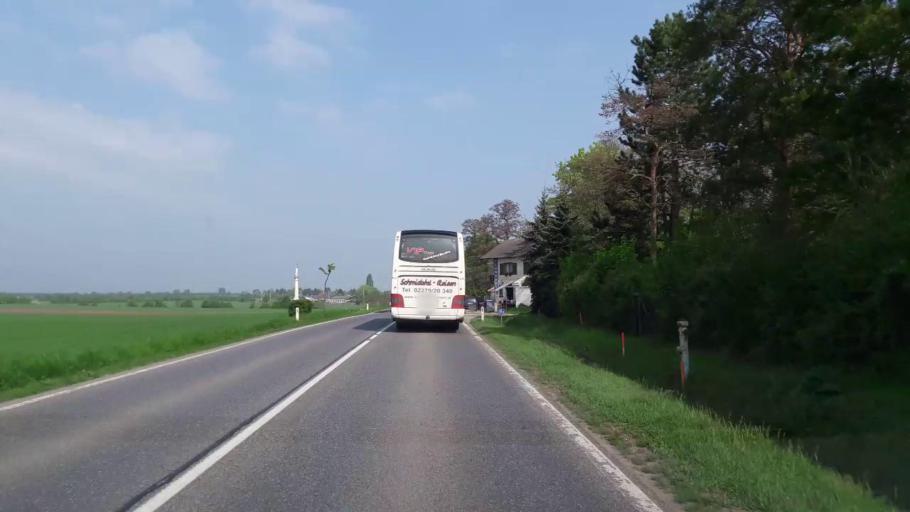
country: AT
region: Lower Austria
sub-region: Politischer Bezirk Hollabrunn
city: Guntersdorf
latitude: 48.6393
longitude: 16.0543
